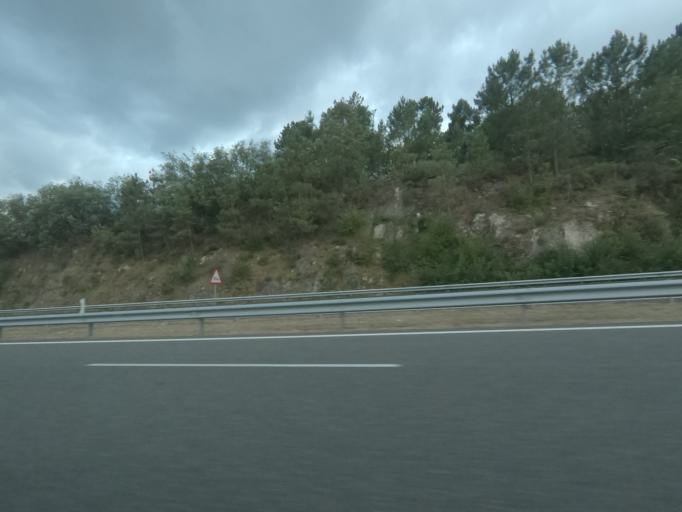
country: ES
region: Galicia
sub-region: Provincia de Ourense
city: Ribadavia
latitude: 42.3021
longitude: -8.1398
